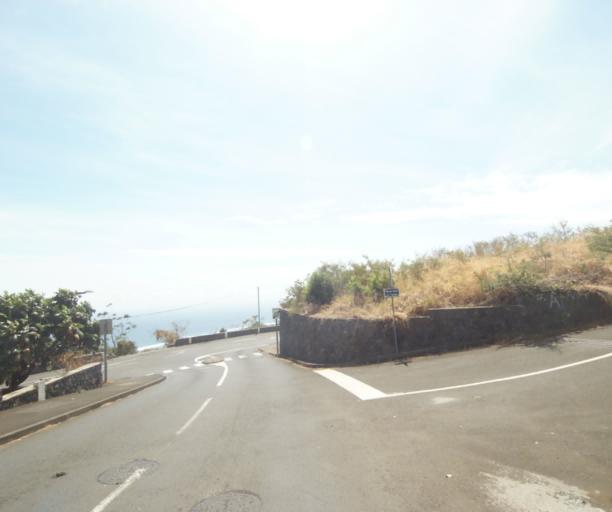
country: RE
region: Reunion
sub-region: Reunion
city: Trois-Bassins
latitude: -21.0996
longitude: 55.2715
